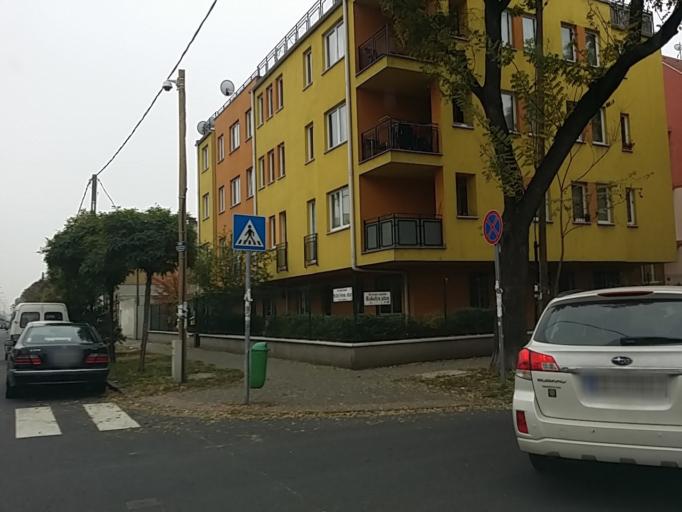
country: HU
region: Budapest
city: Budapest XIII. keruelet
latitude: 47.5416
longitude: 19.0918
